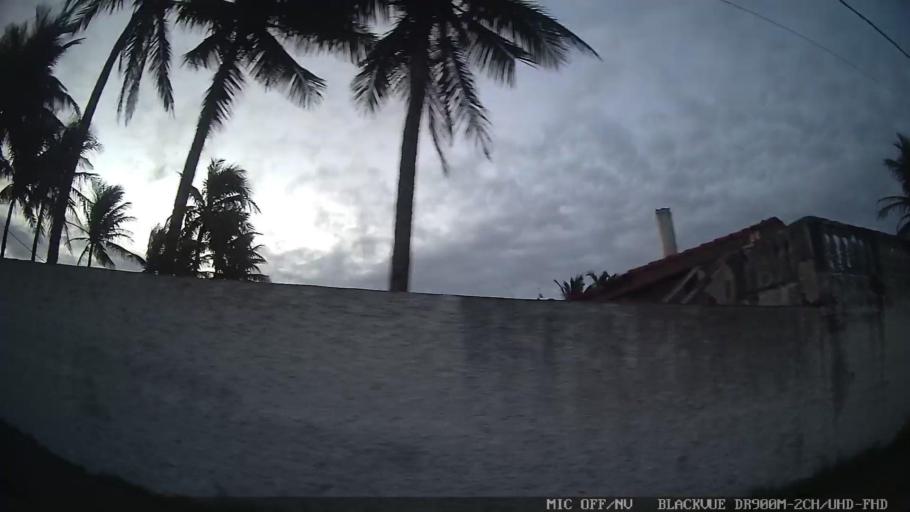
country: BR
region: Sao Paulo
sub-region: Itanhaem
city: Itanhaem
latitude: -24.2468
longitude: -46.8903
